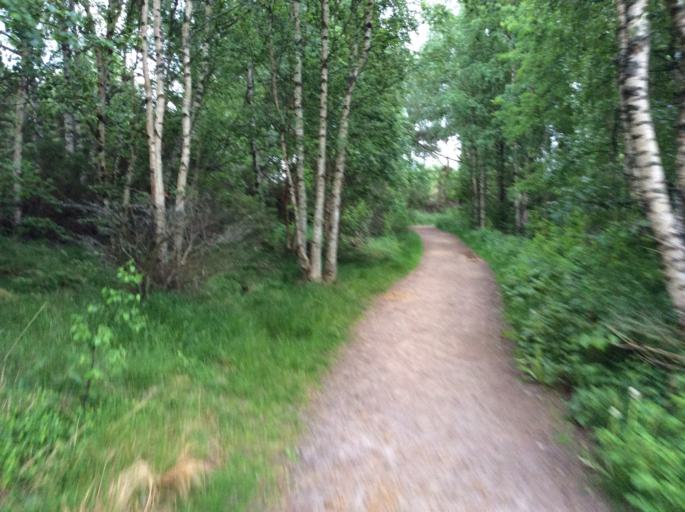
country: SE
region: Vaestra Goetaland
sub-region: Goteborg
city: Majorna
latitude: 57.7996
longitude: 11.8824
